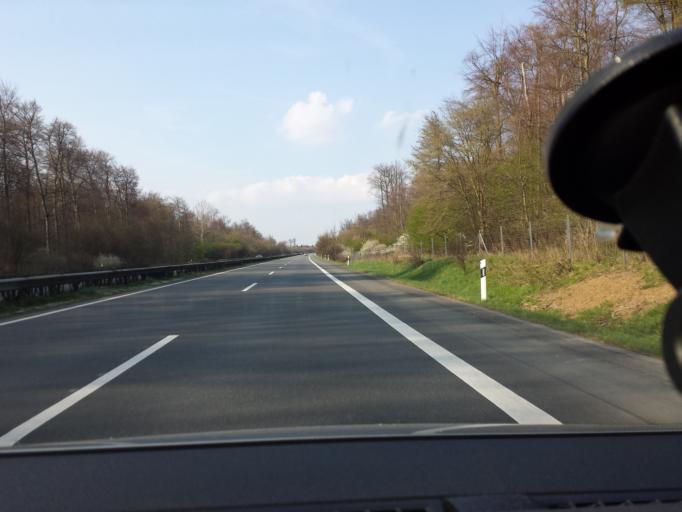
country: DE
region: Lower Saxony
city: Flothe
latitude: 52.1121
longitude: 10.4880
